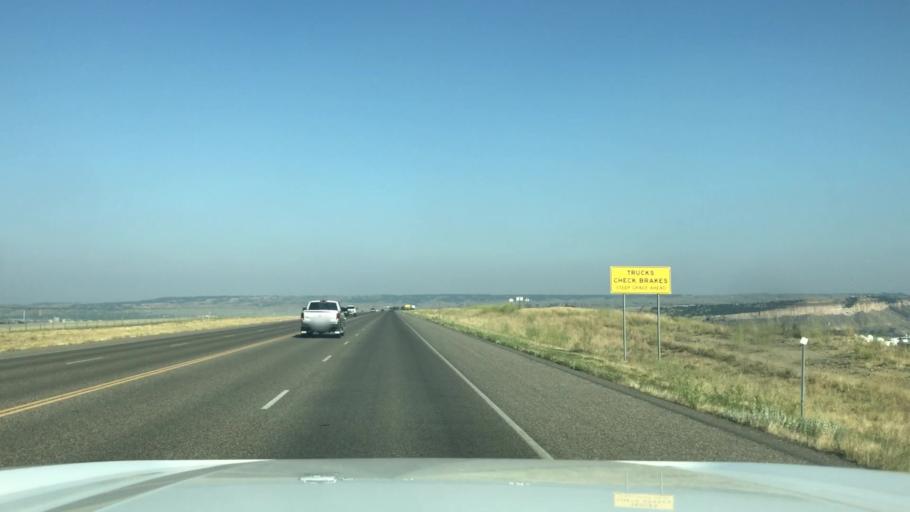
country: US
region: Montana
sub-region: Yellowstone County
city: Billings
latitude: 45.8003
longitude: -108.5189
